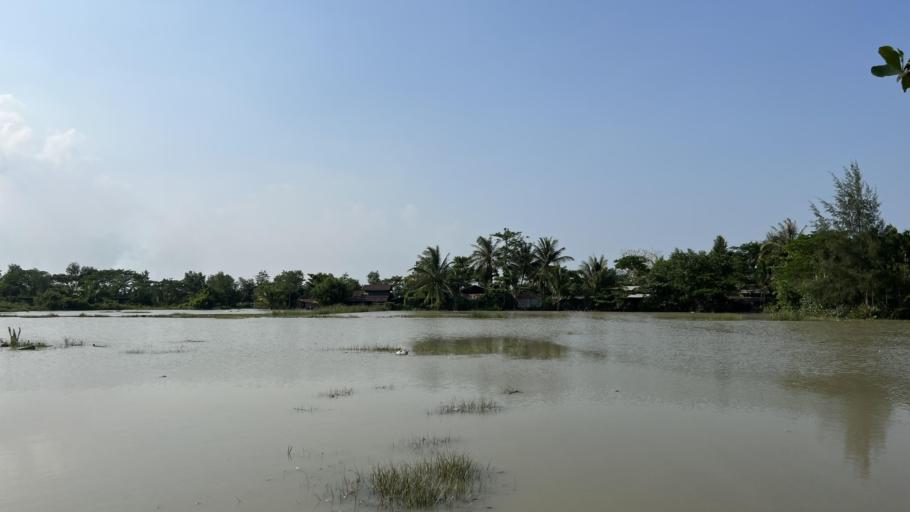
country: MM
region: Ayeyarwady
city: Pyapon
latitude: 16.1779
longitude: 95.6921
